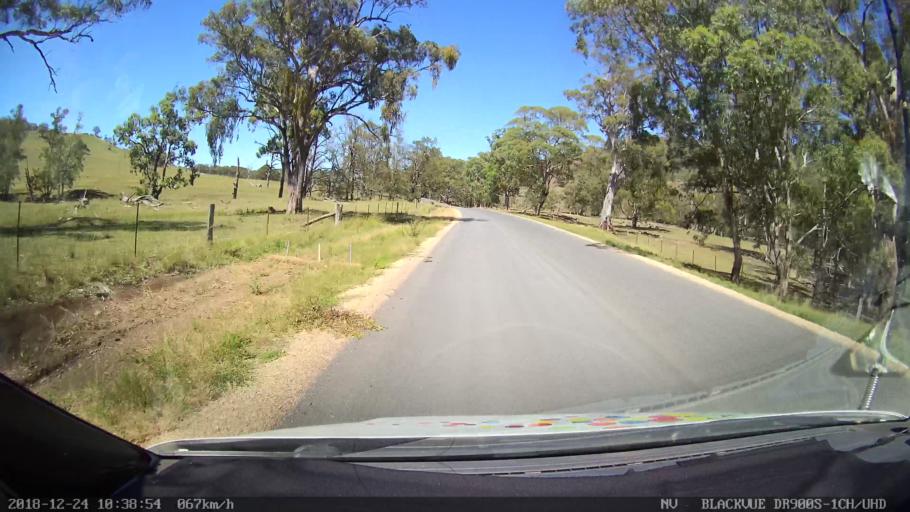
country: AU
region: New South Wales
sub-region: Upper Hunter Shire
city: Merriwa
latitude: -31.8501
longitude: 150.4789
